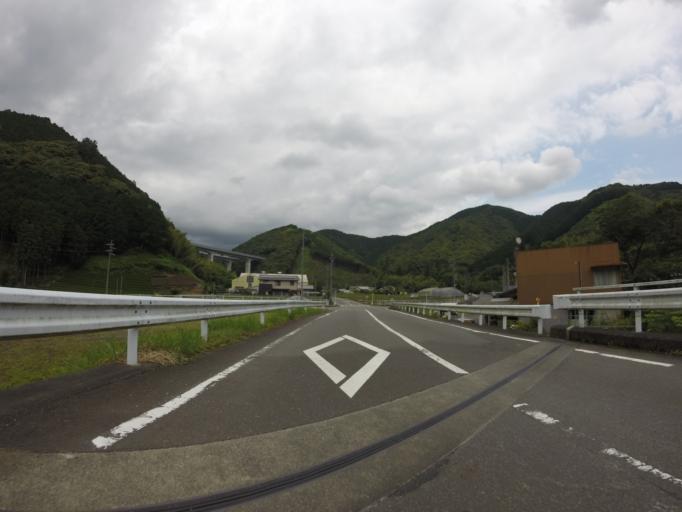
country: JP
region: Shizuoka
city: Shizuoka-shi
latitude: 35.0039
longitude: 138.3138
